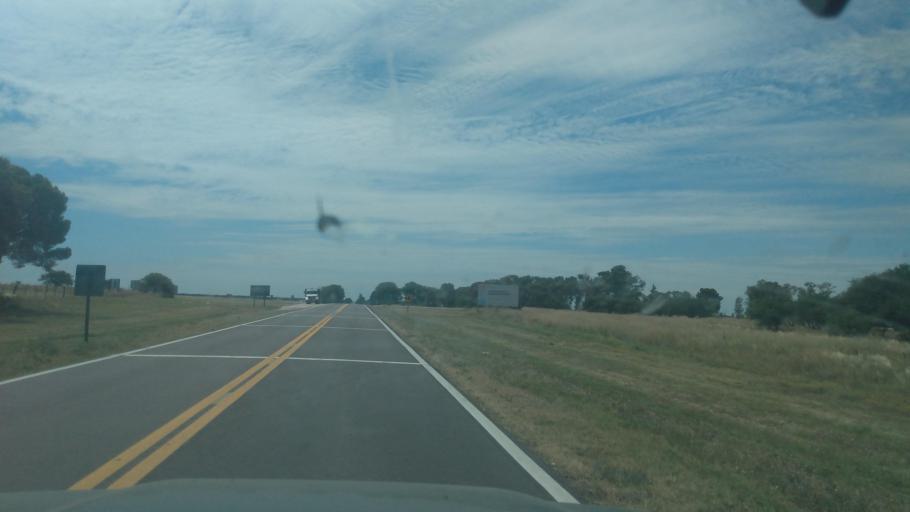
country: AR
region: La Pampa
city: Doblas
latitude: -37.1225
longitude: -64.2859
